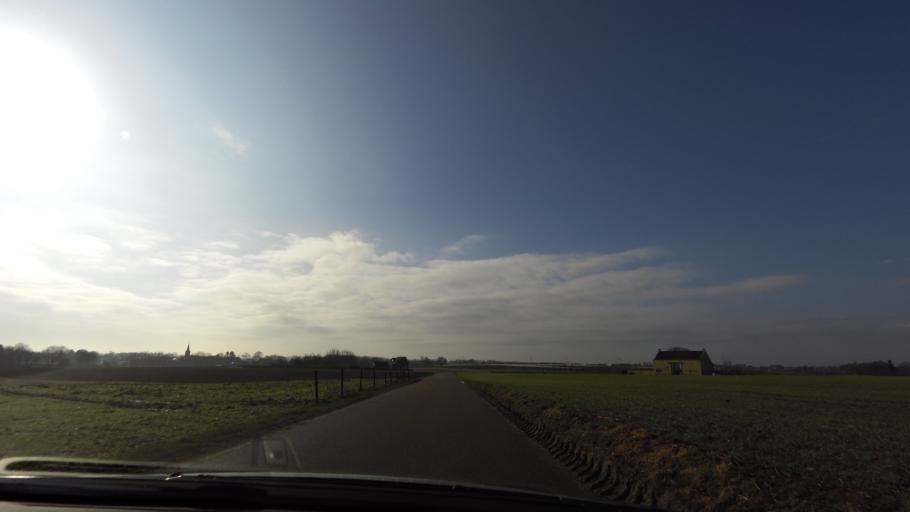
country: NL
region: Limburg
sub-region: Valkenburg aan de Geul
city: Sibbe
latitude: 50.8351
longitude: 5.8361
